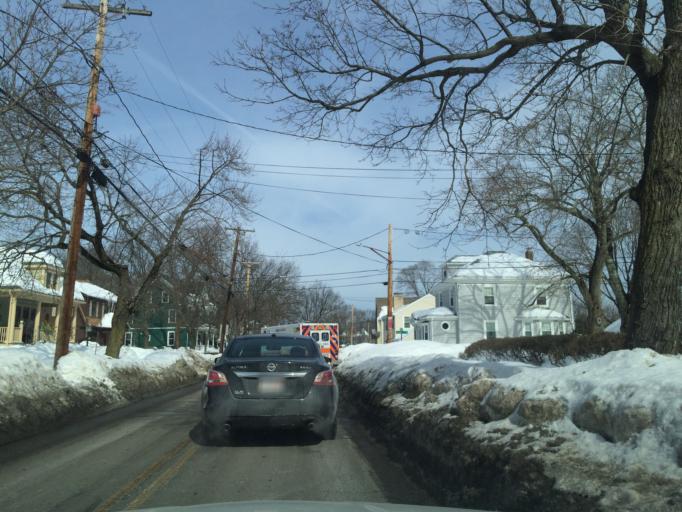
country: US
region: Massachusetts
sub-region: Middlesex County
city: Waltham
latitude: 42.3511
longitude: -71.2390
